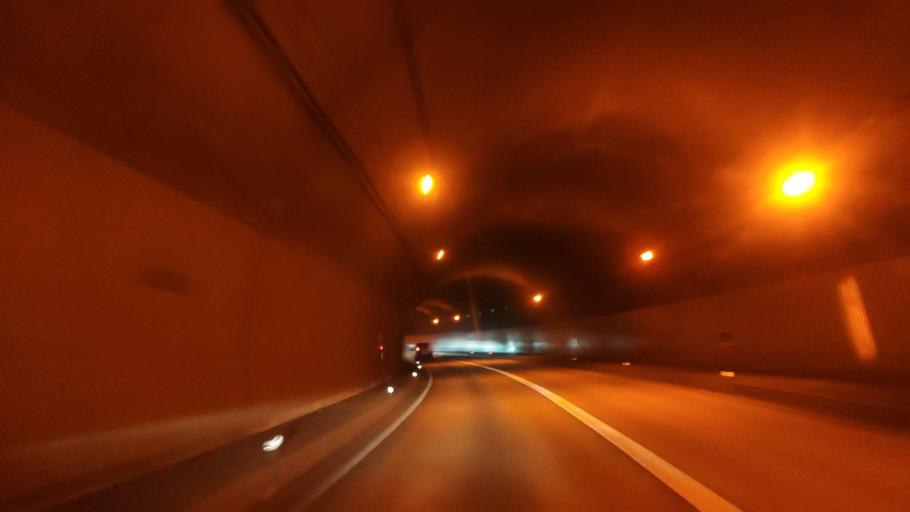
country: JP
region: Nagano
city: Okaya
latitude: 36.0894
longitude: 138.0607
